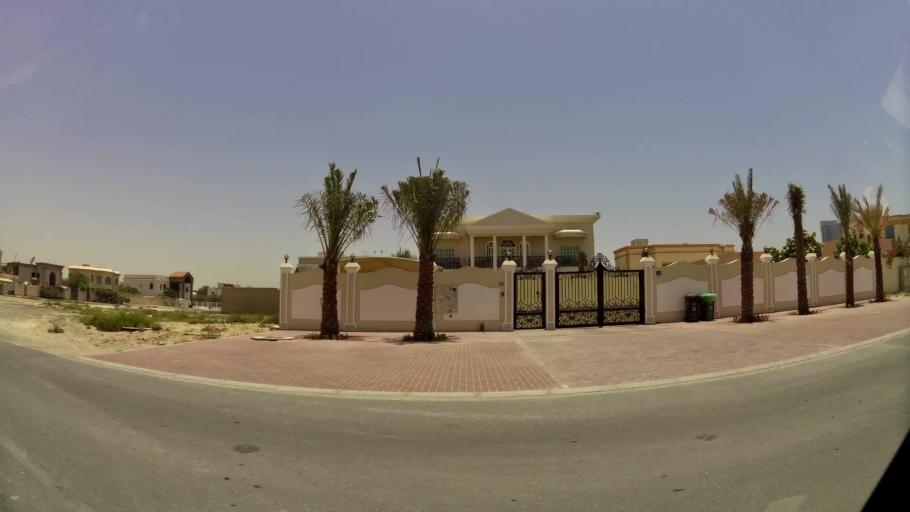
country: AE
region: Dubai
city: Dubai
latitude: 25.0972
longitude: 55.1911
